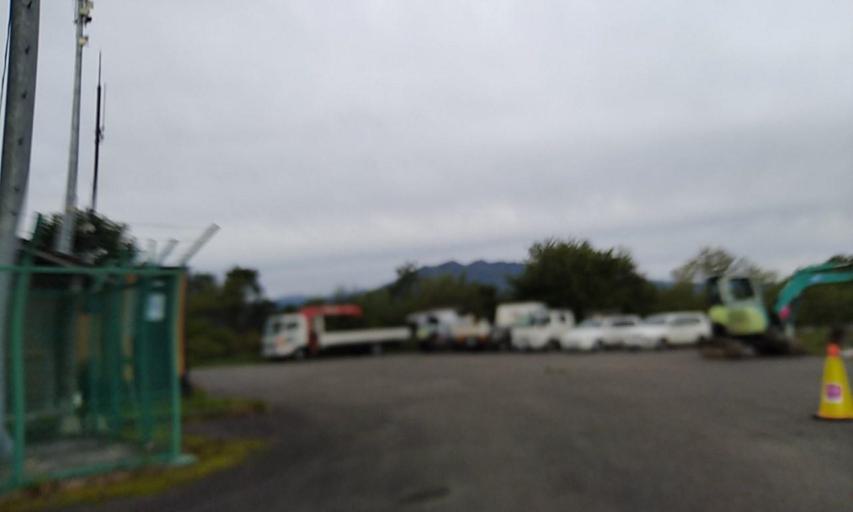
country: JP
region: Hokkaido
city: Obihiro
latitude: 42.8293
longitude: 142.9811
